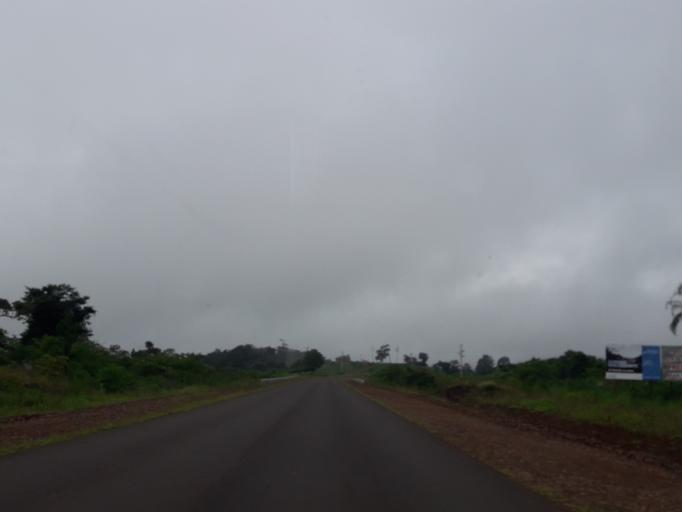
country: AR
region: Misiones
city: Bernardo de Irigoyen
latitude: -26.4132
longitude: -53.8235
